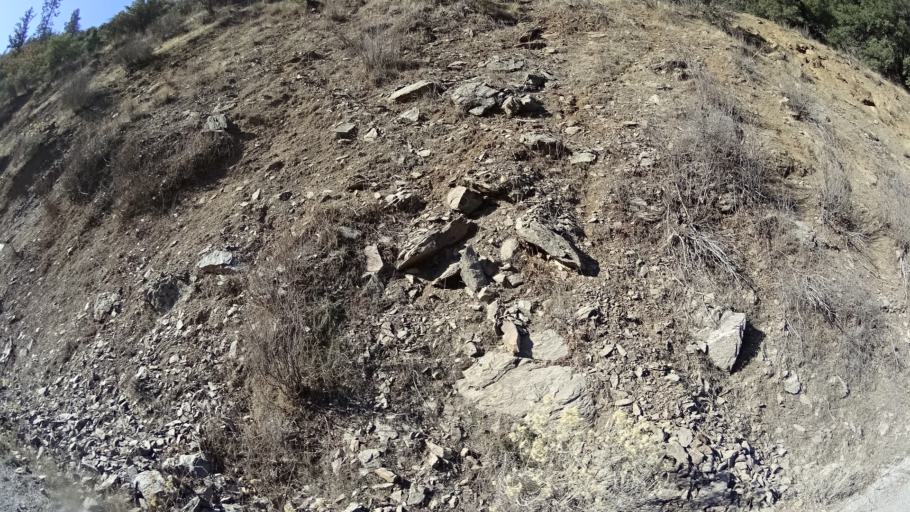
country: US
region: California
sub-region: Siskiyou County
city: Yreka
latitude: 41.8295
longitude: -122.6621
